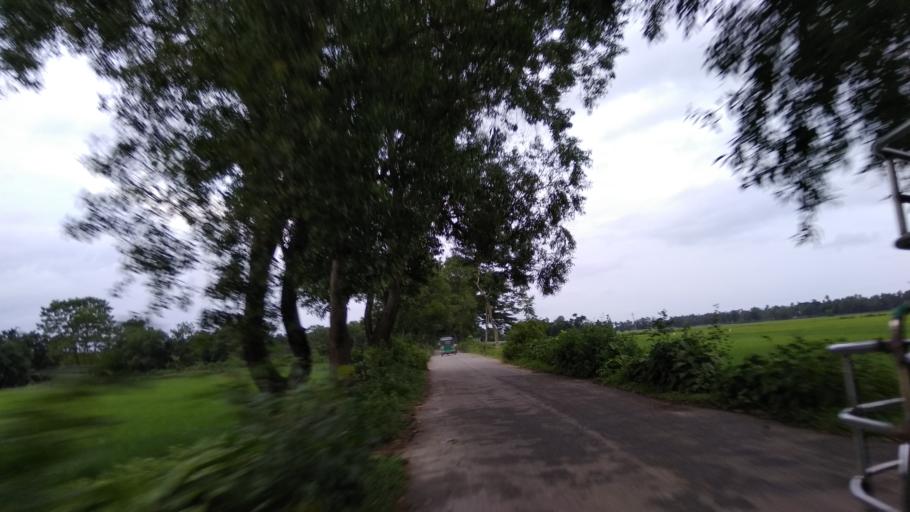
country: IN
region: Tripura
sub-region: Dhalai
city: Kamalpur
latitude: 24.2180
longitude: 91.8545
